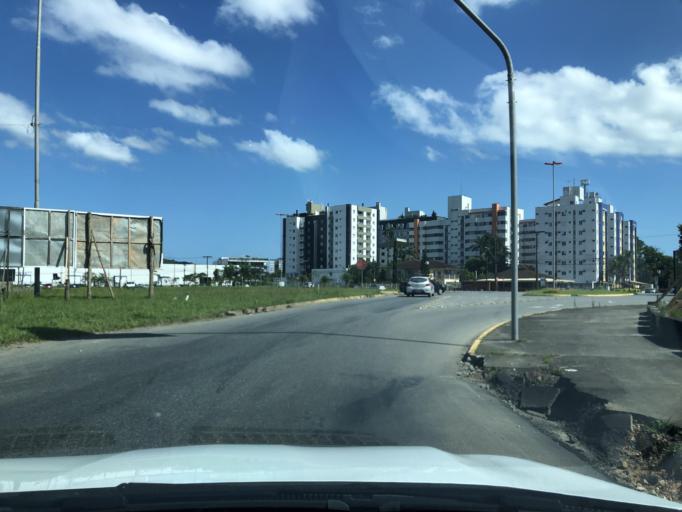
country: BR
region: Santa Catarina
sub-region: Joinville
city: Joinville
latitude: -26.2499
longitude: -48.8544
